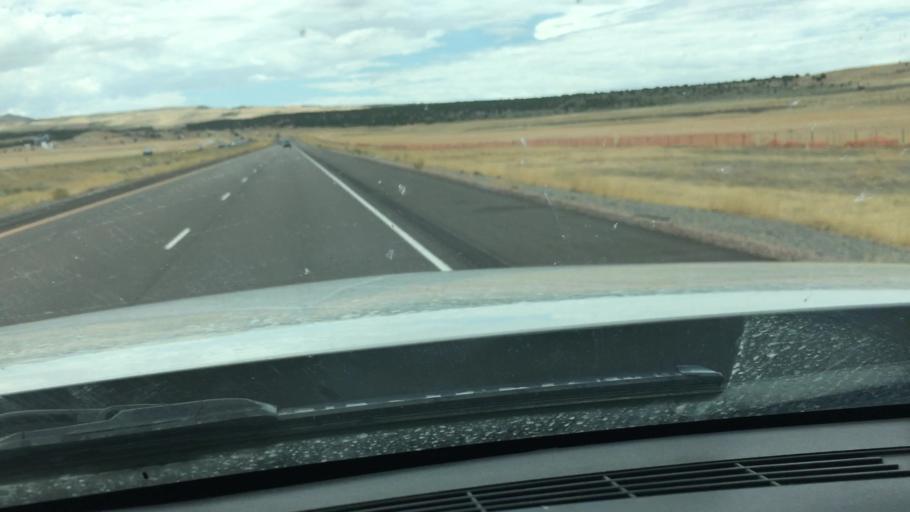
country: US
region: Utah
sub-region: Millard County
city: Fillmore
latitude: 38.7420
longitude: -112.5807
